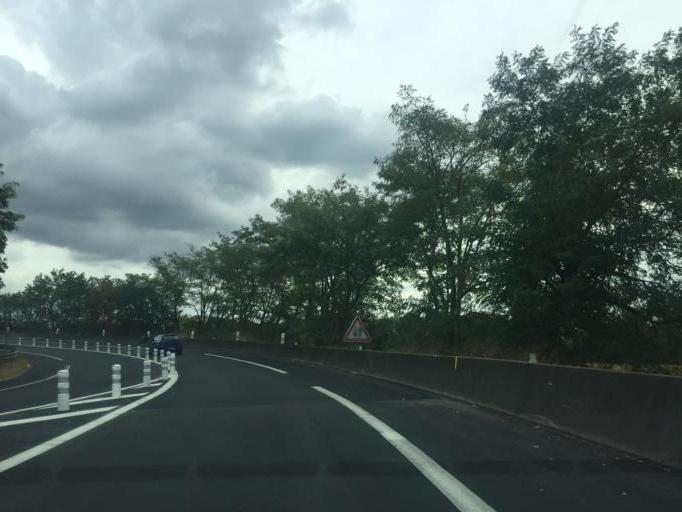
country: FR
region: Rhone-Alpes
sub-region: Departement de l'Ain
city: Saint-Maurice-de-Beynost
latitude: 45.8171
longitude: 4.9843
